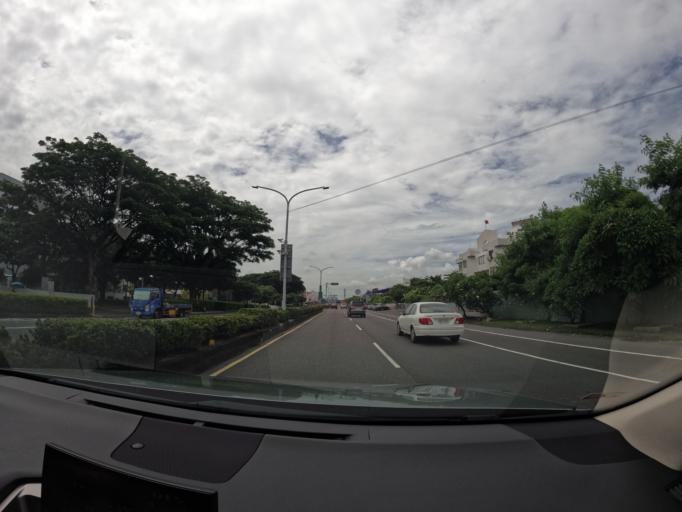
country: TW
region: Kaohsiung
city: Kaohsiung
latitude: 22.7838
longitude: 120.2973
